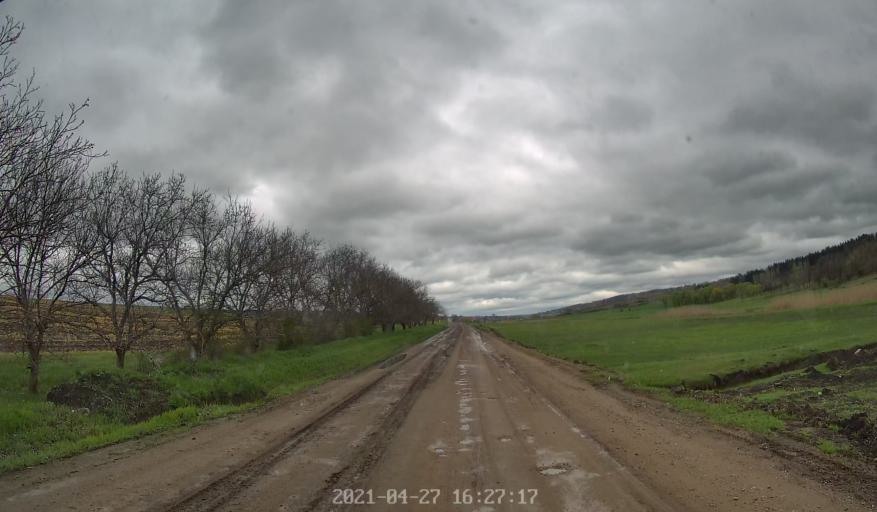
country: MD
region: Chisinau
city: Singera
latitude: 46.9761
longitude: 29.0327
